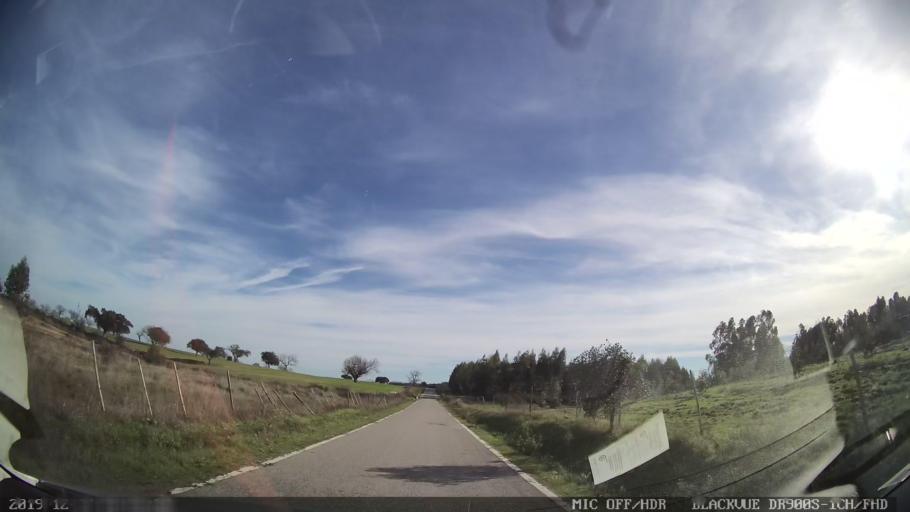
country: PT
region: Portalegre
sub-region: Nisa
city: Nisa
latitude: 39.4966
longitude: -7.7568
